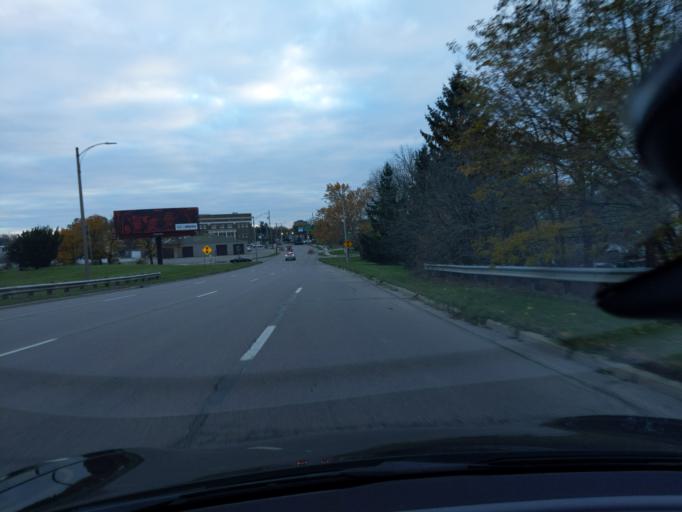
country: US
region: Michigan
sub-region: Ingham County
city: Lansing
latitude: 42.7496
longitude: -84.5461
